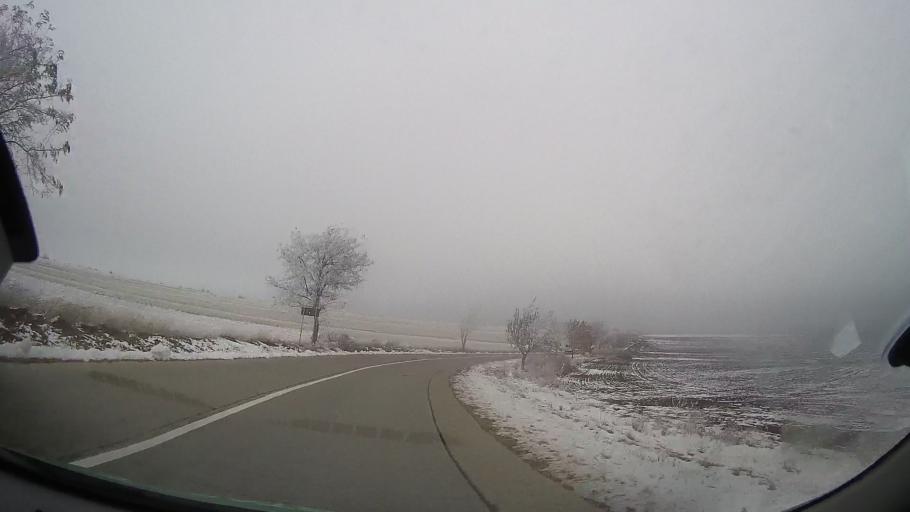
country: RO
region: Vaslui
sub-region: Comuna Ivesti
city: Ivesti
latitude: 46.1978
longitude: 27.5923
